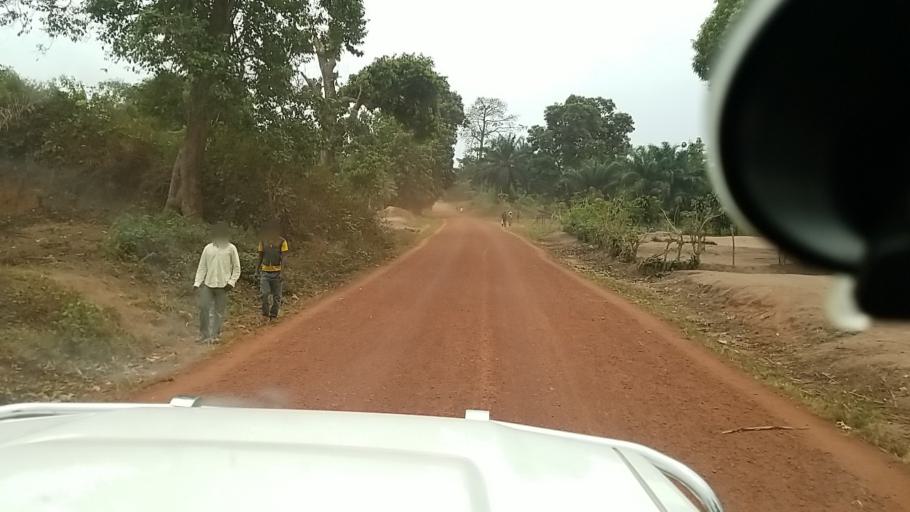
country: CD
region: Equateur
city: Libenge
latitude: 3.7255
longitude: 18.7712
